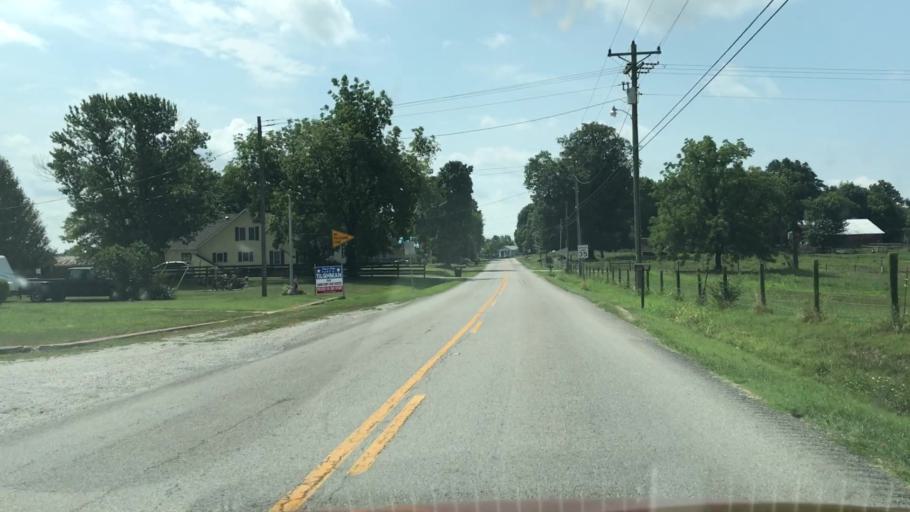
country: US
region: Kentucky
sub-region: Barren County
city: Glasgow
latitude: 36.8924
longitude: -85.8555
